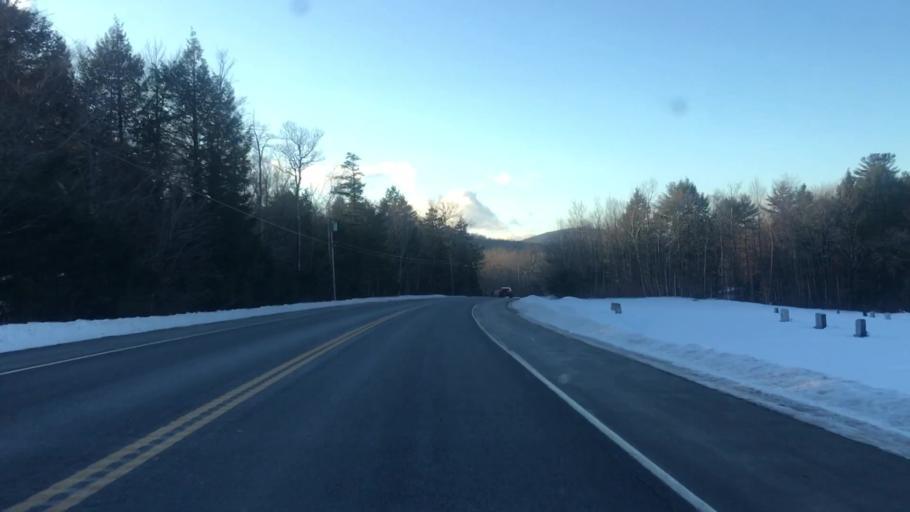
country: US
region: Maine
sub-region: Franklin County
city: Wilton
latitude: 44.5846
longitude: -70.2447
